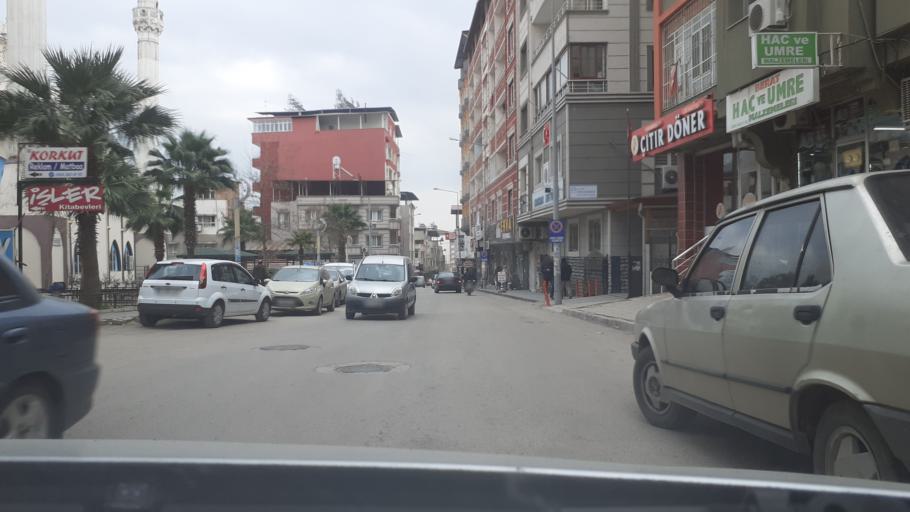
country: TR
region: Hatay
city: Kirikhan
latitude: 36.4979
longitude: 36.3541
